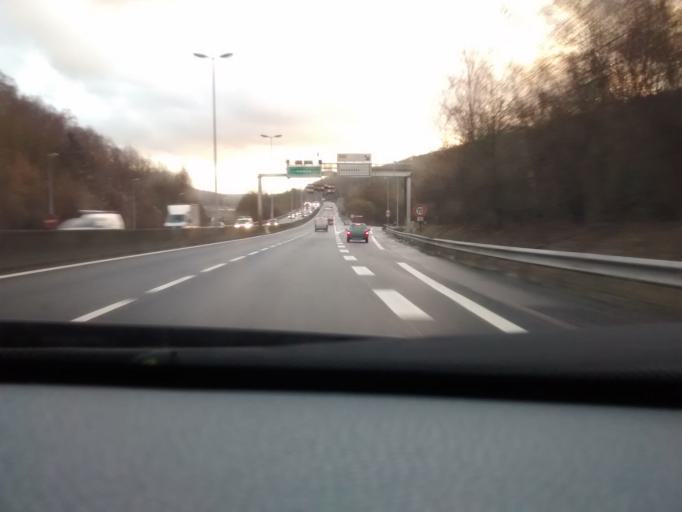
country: FR
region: Haute-Normandie
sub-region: Departement de la Seine-Maritime
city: Darnetal
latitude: 49.4587
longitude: 1.1437
